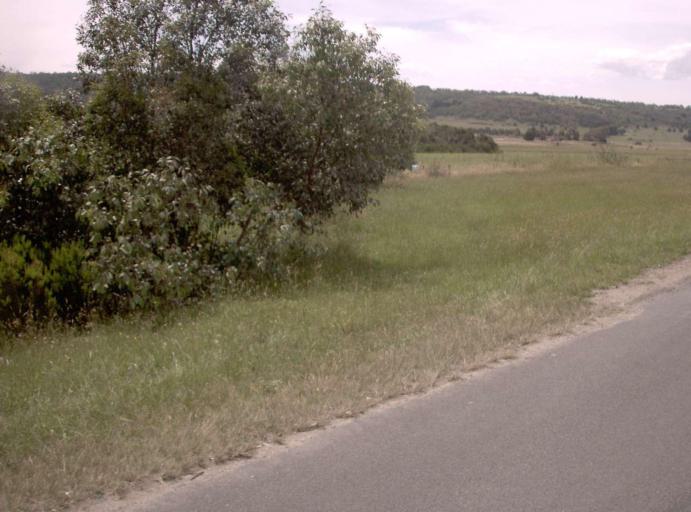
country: AU
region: Victoria
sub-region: Mornington Peninsula
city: Safety Beach
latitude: -38.3138
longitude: 145.0151
